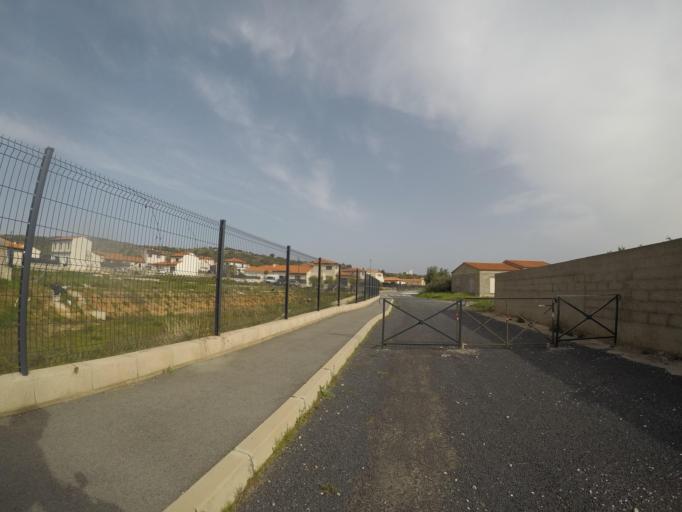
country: FR
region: Languedoc-Roussillon
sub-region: Departement des Pyrenees-Orientales
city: Baixas
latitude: 42.7548
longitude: 2.8135
